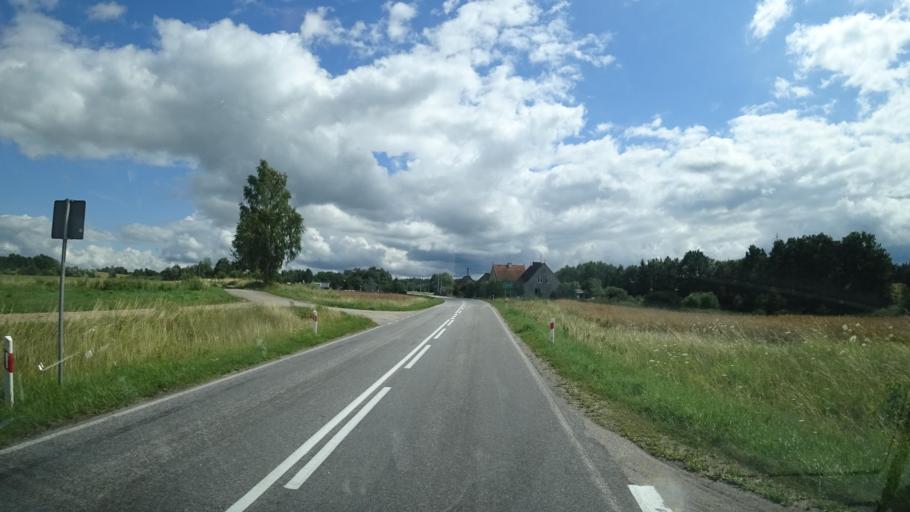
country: PL
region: Warmian-Masurian Voivodeship
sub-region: Powiat goldapski
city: Banie Mazurskie
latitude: 54.2142
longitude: 22.1643
